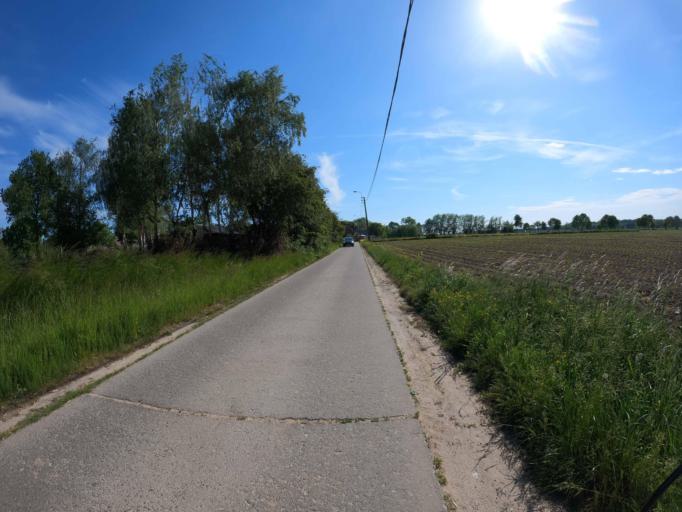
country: BE
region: Flanders
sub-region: Provincie Oost-Vlaanderen
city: Oosterzele
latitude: 50.9200
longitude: 3.7835
